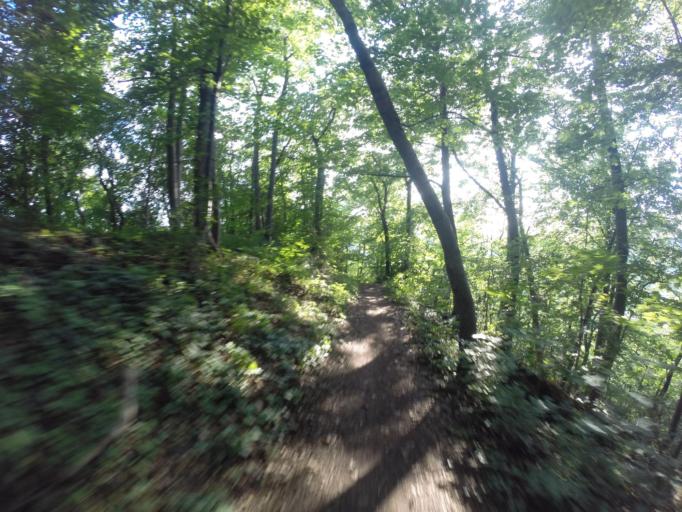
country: DE
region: Thuringia
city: Golmsdorf
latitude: 50.9605
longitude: 11.6478
